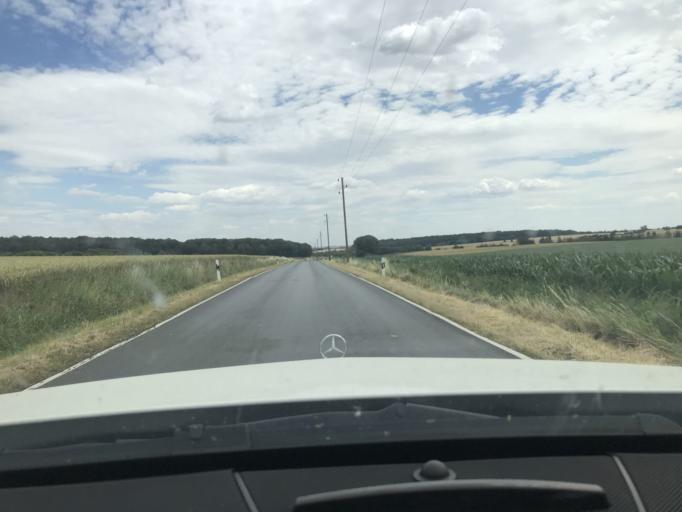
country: DE
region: Thuringia
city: Holzsussra
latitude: 51.2975
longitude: 10.6545
